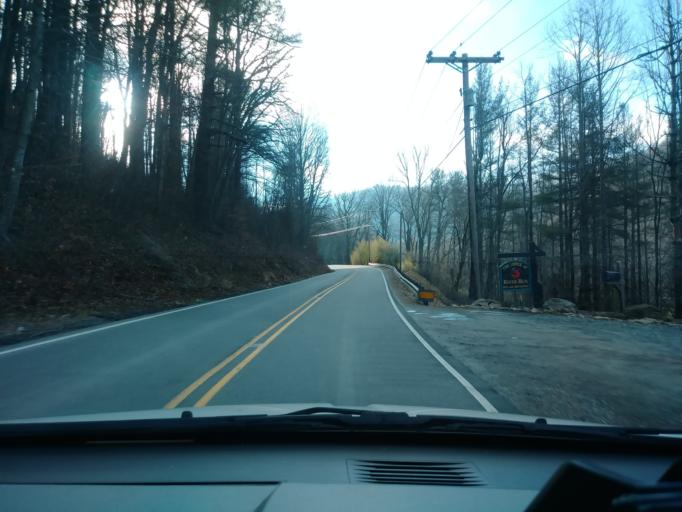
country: US
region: North Carolina
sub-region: Avery County
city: Banner Elk
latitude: 36.1768
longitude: -81.9208
